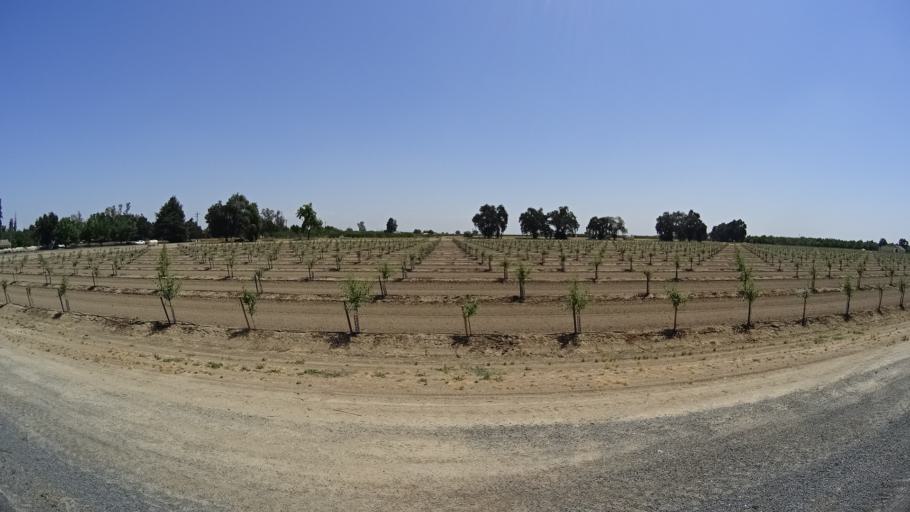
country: US
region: California
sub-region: Fresno County
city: Laton
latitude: 36.4149
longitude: -119.6728
